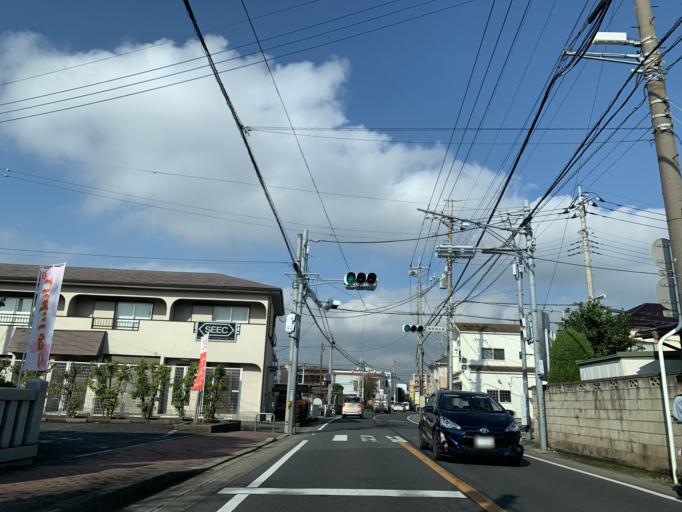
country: JP
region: Chiba
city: Noda
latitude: 35.9124
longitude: 139.9051
